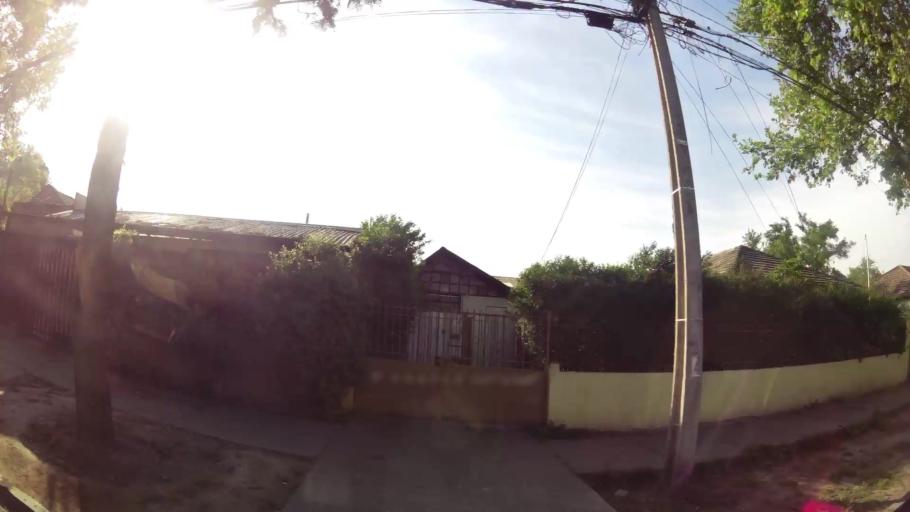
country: CL
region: Santiago Metropolitan
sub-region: Provincia de Santiago
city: Santiago
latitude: -33.5072
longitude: -70.6651
